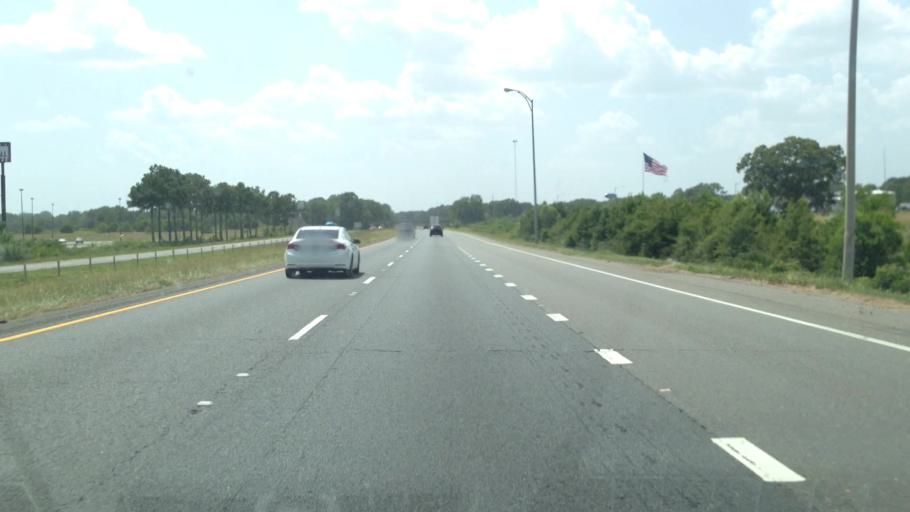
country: US
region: Louisiana
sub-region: Bienville Parish
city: Arcadia
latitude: 32.5643
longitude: -92.9133
